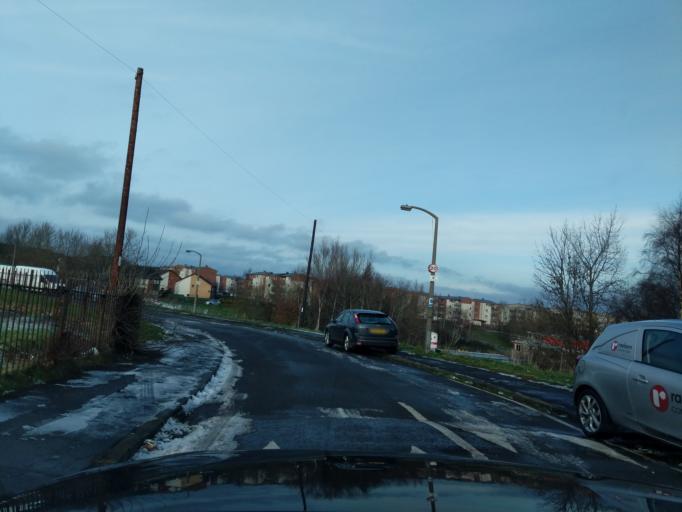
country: GB
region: Scotland
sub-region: Midlothian
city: Loanhead
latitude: 55.8973
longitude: -3.1549
